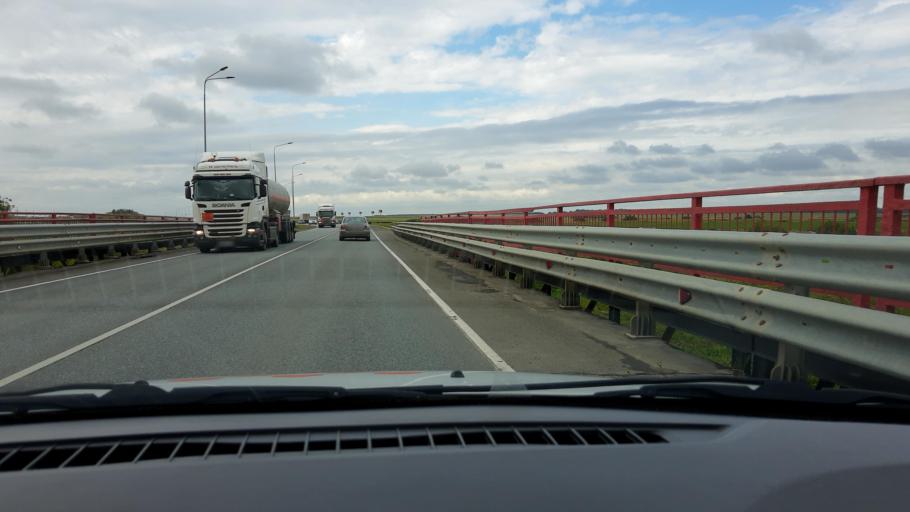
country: RU
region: Tatarstan
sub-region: Alekseyevskiy Rayon
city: Alekseyevskoye
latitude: 55.3117
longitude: 50.2960
